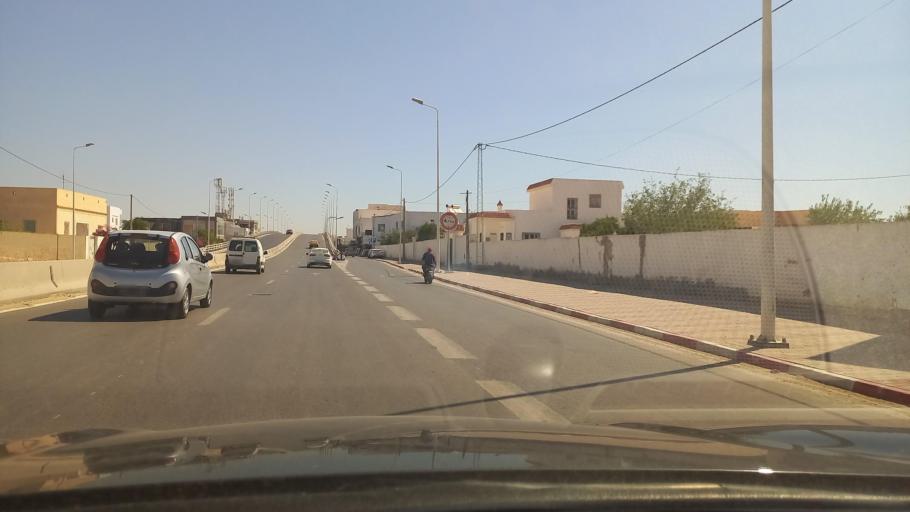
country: TN
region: Safaqis
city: Sfax
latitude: 34.7545
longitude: 10.7329
